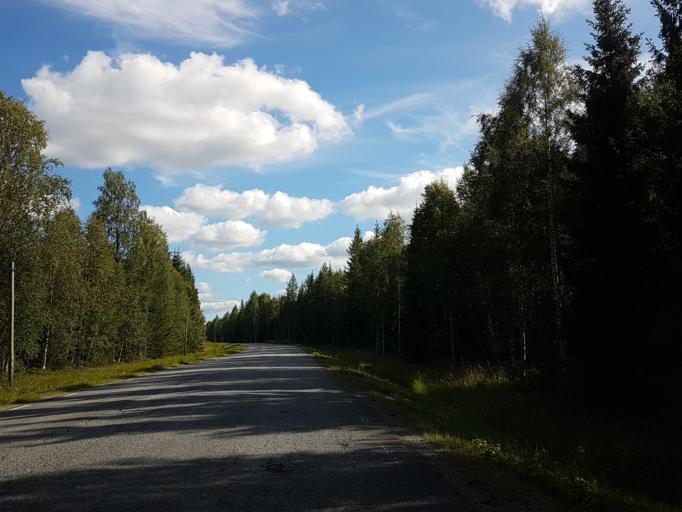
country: SE
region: Vaesterbotten
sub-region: Skelleftea Kommun
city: Burtraesk
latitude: 64.3276
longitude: 20.5262
